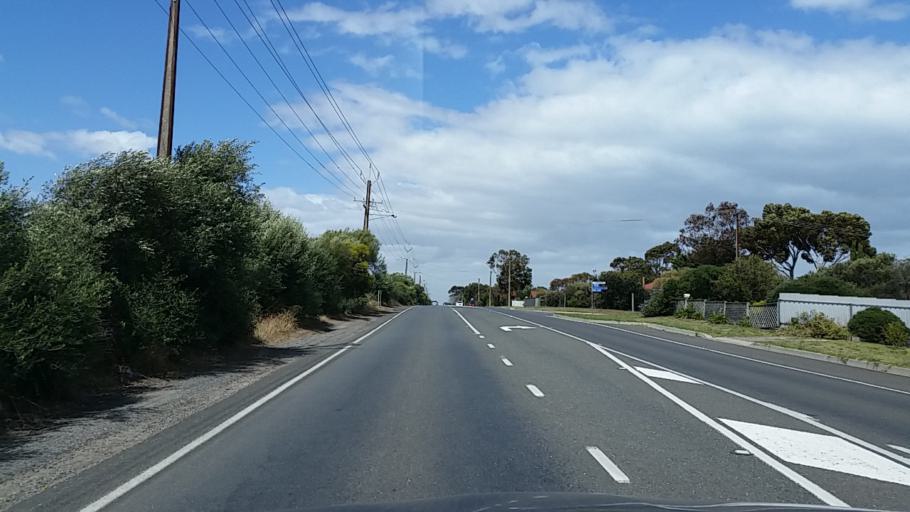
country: AU
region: South Australia
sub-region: Alexandrina
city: Port Elliot
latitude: -35.5204
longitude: 138.6755
